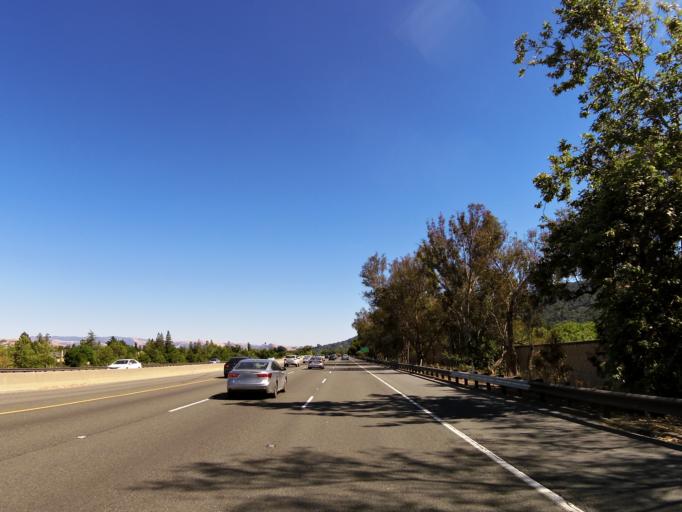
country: US
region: California
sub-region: Alameda County
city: Pleasanton
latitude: 37.6704
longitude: -121.9109
